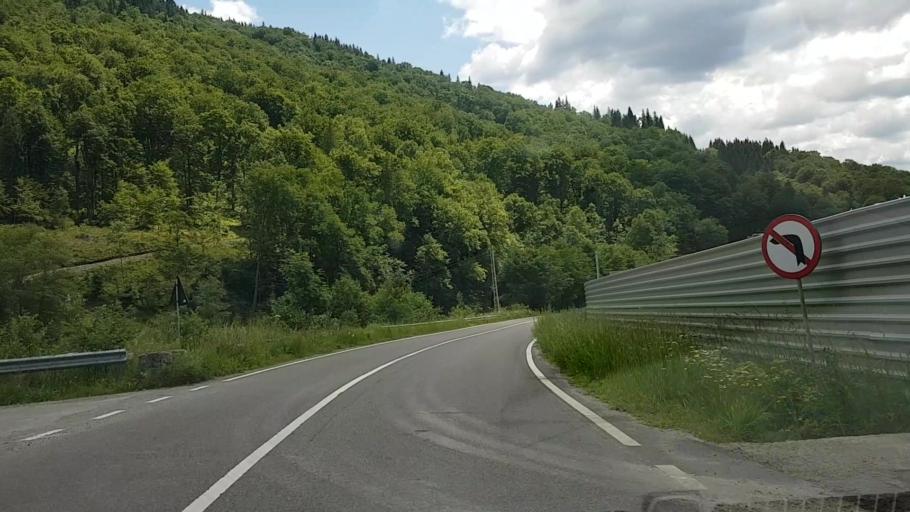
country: RO
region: Suceava
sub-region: Comuna Crucea
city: Crucea
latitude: 47.3220
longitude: 25.6263
